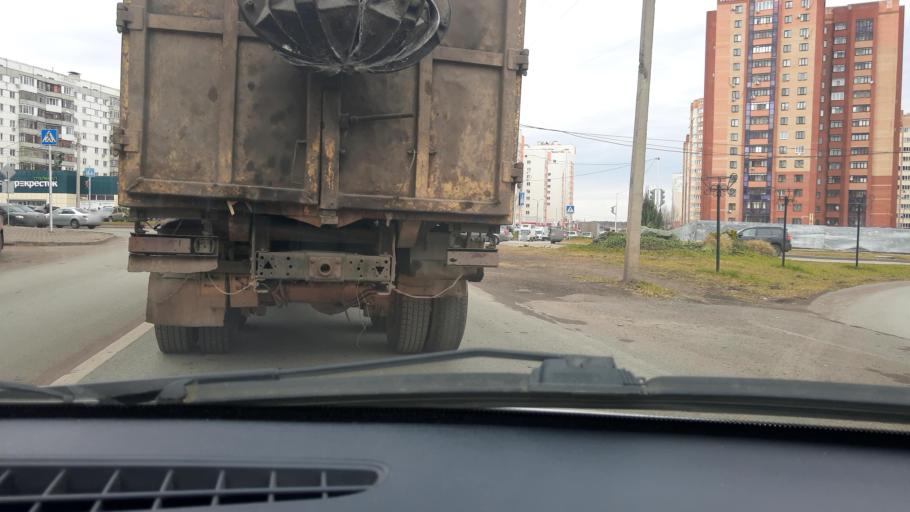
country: RU
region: Bashkortostan
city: Mikhaylovka
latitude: 54.7101
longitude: 55.8365
